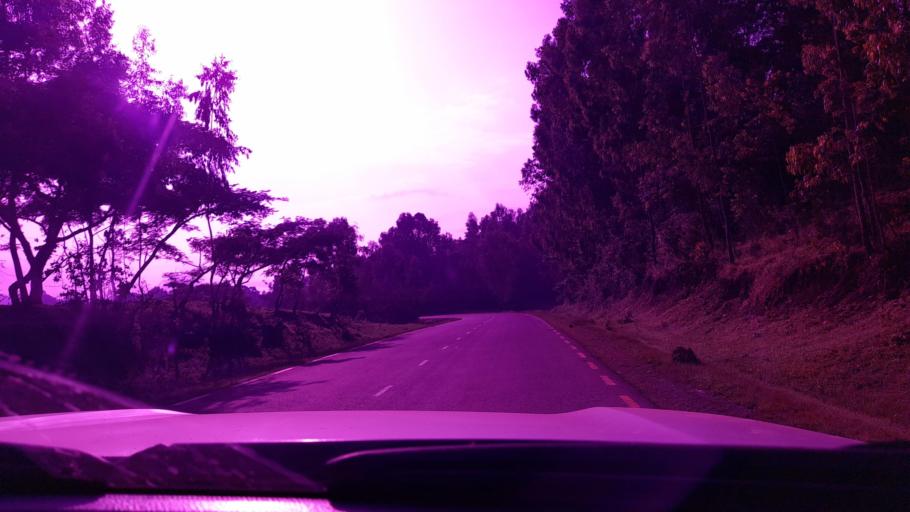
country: ET
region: Oromiya
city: Bedele
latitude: 8.1504
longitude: 36.4630
